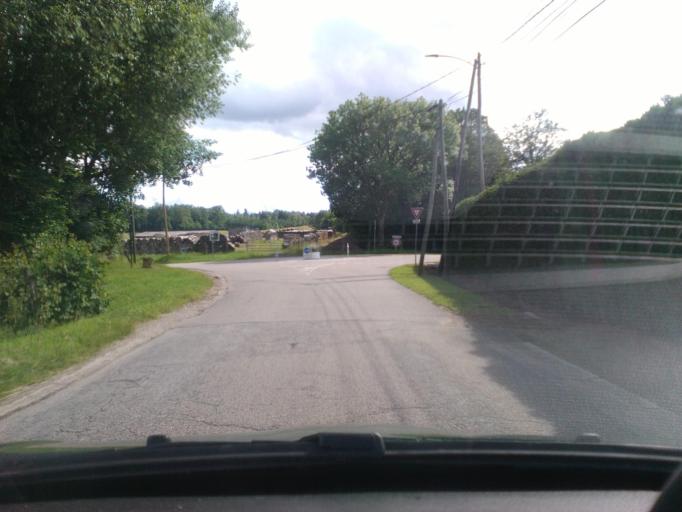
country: FR
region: Lorraine
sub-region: Departement des Vosges
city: Bruyeres
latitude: 48.2196
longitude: 6.7579
